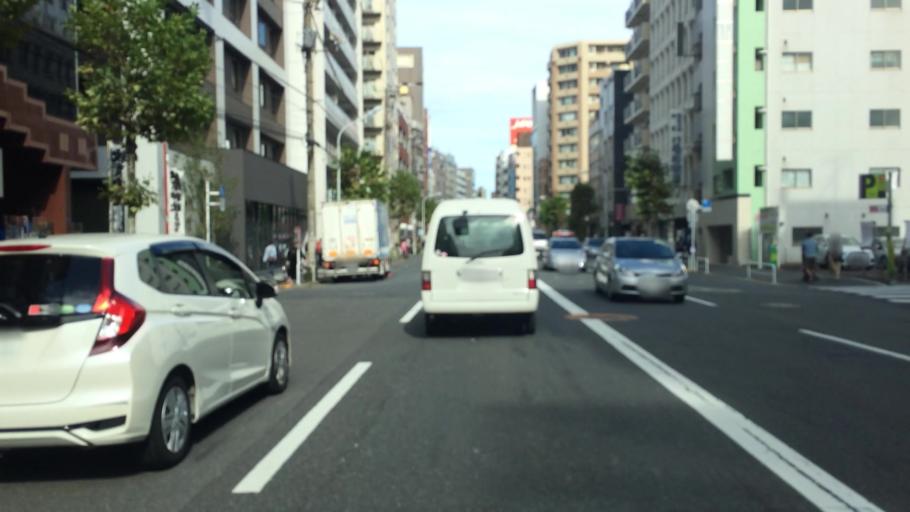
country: JP
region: Tokyo
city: Tokyo
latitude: 35.7057
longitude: 139.7817
